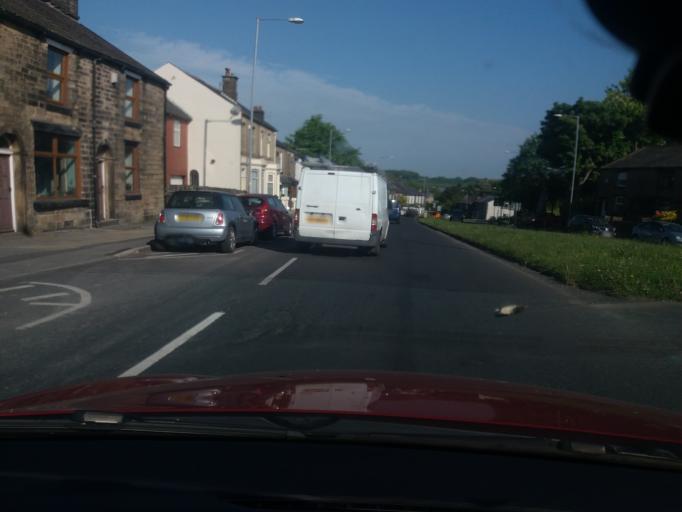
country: GB
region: England
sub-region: Borough of Bolton
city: Horwich
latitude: 53.6022
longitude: -2.5547
